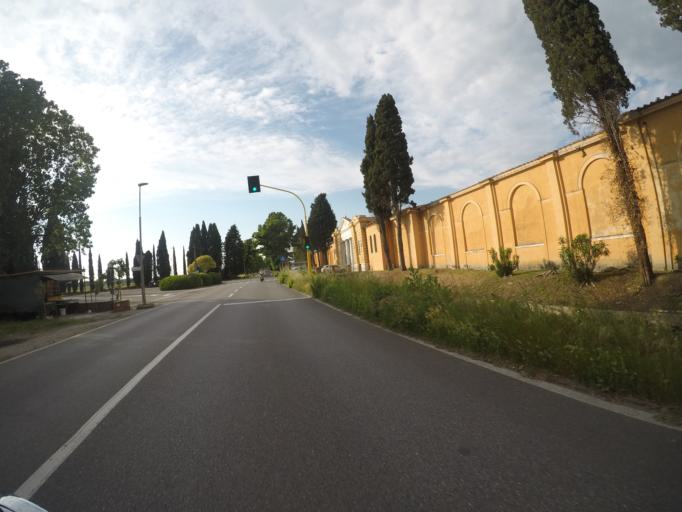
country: IT
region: Tuscany
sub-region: Province of Pisa
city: Madonna dell'Acqua
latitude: 43.7332
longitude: 10.3852
